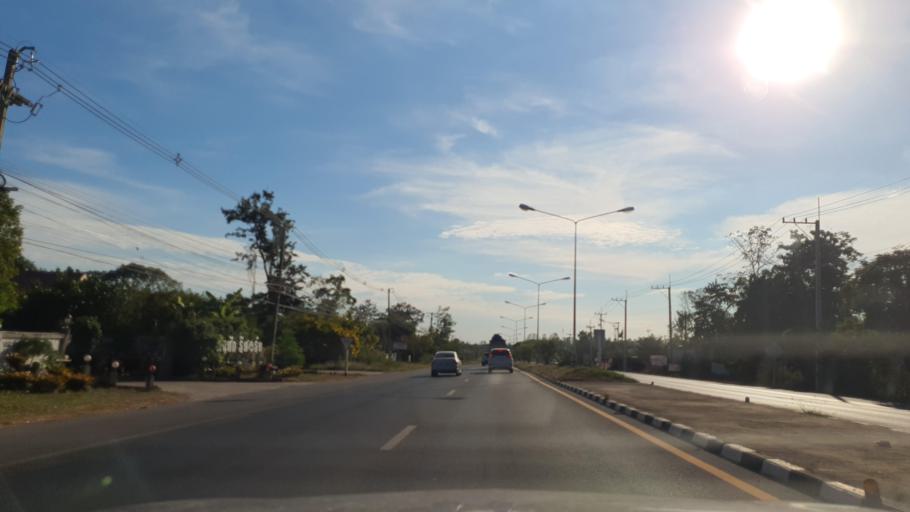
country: TH
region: Kalasin
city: Yang Talat
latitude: 16.3678
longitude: 103.3432
